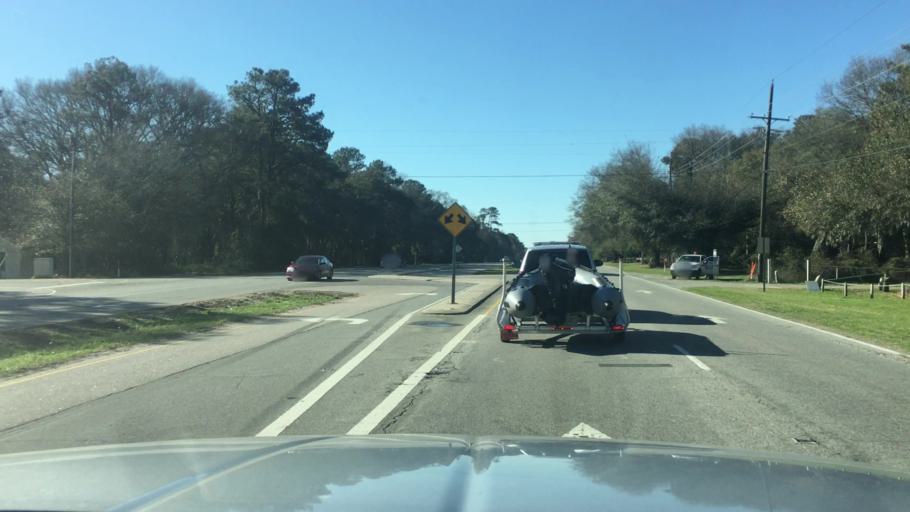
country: US
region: North Carolina
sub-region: New Hanover County
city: Sea Breeze
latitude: 34.0739
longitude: -77.8955
